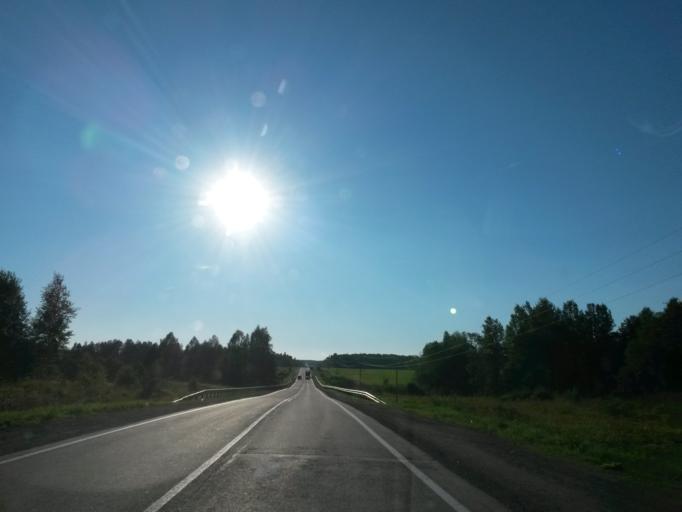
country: RU
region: Jaroslavl
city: Gavrilov-Yam
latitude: 57.2628
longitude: 40.0314
